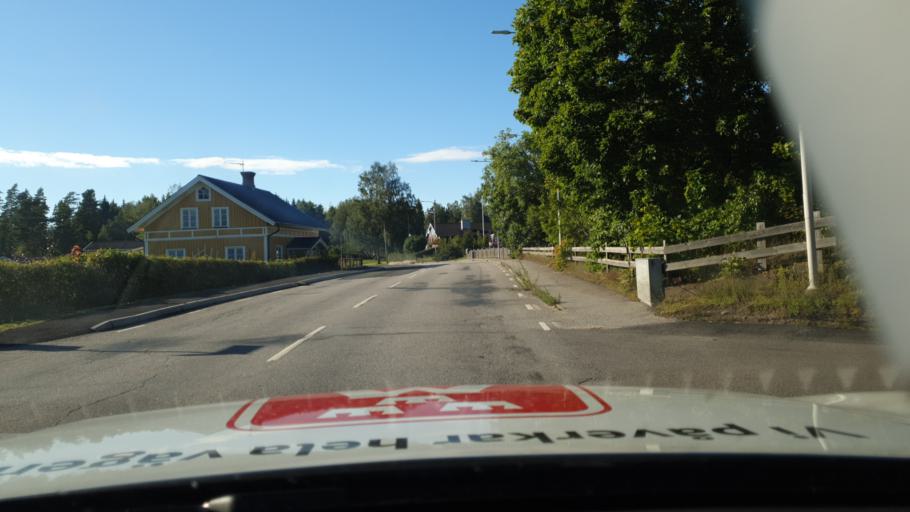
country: SE
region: Vaestra Goetaland
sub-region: Toreboda Kommun
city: Toereboda
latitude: 58.8068
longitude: 14.0585
